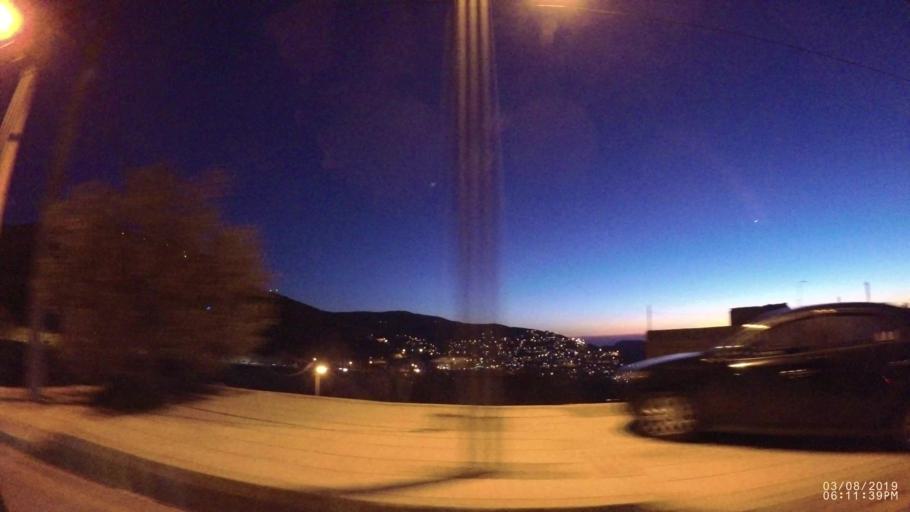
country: JO
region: Ma'an
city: Petra
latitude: 30.3282
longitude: 35.4908
